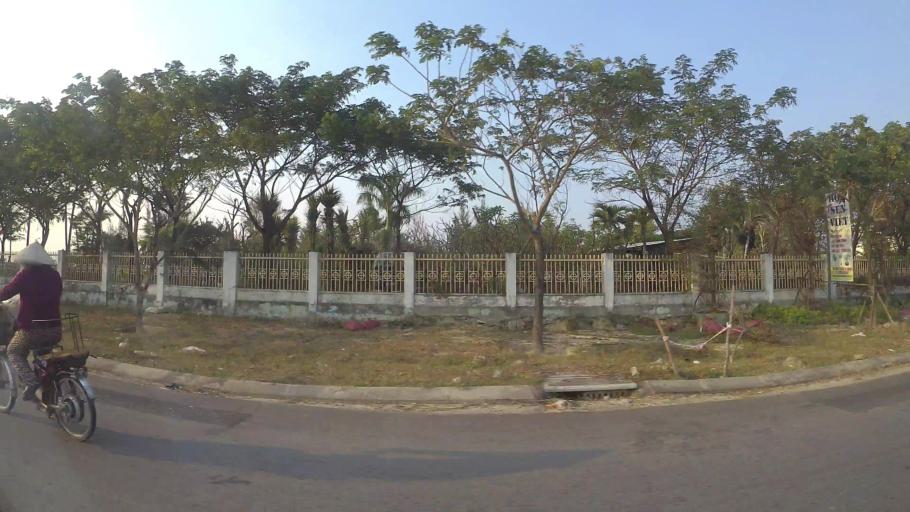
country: VN
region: Da Nang
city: Ngu Hanh Son
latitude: 15.9780
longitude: 108.2441
